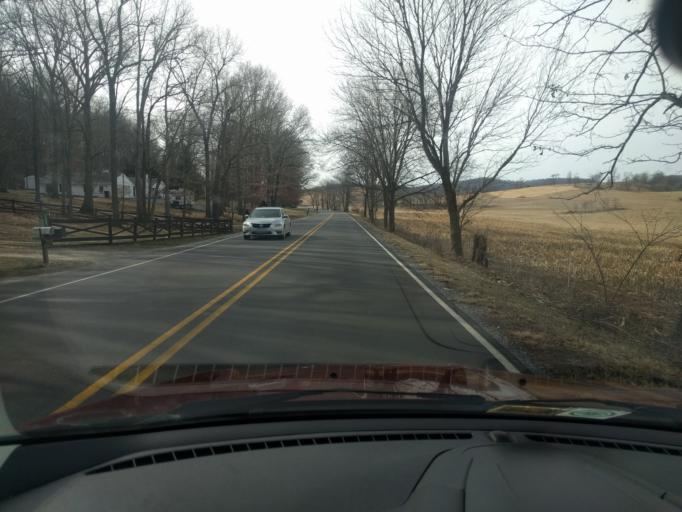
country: US
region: Virginia
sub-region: Augusta County
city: Stuarts Draft
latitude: 38.0429
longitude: -79.1004
